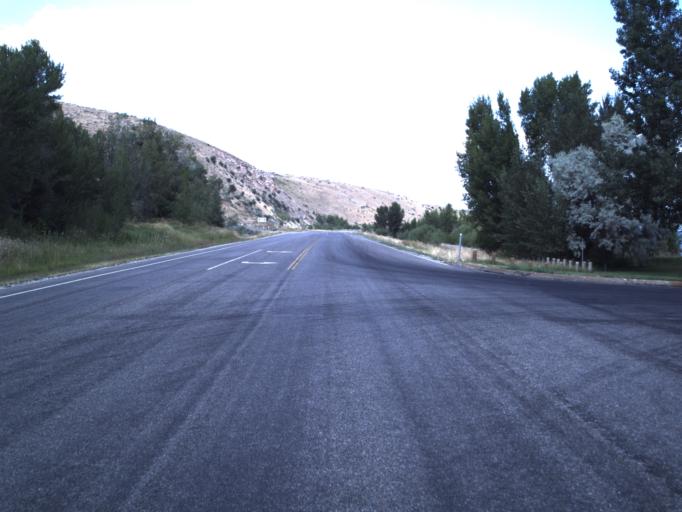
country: US
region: Utah
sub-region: Rich County
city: Randolph
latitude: 41.8571
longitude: -111.3644
